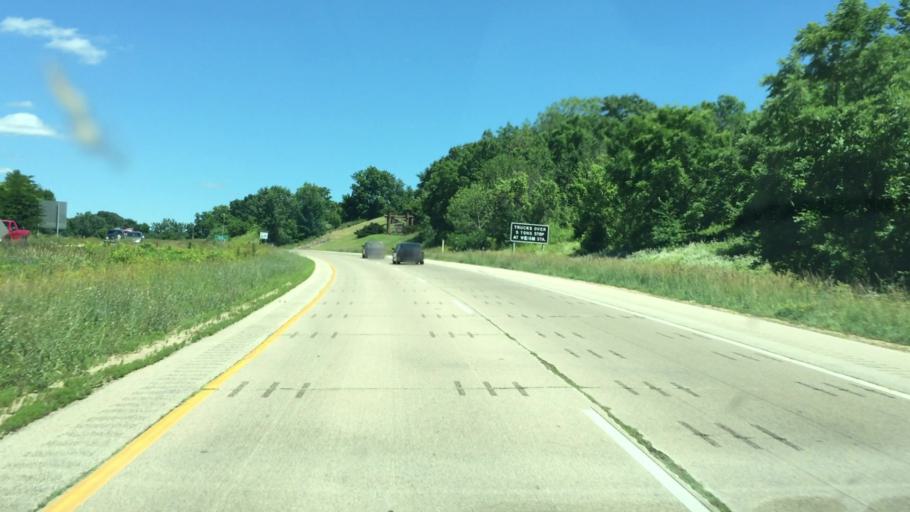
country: US
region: Illinois
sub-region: Jo Daviess County
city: East Dubuque
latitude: 42.5152
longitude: -90.6221
